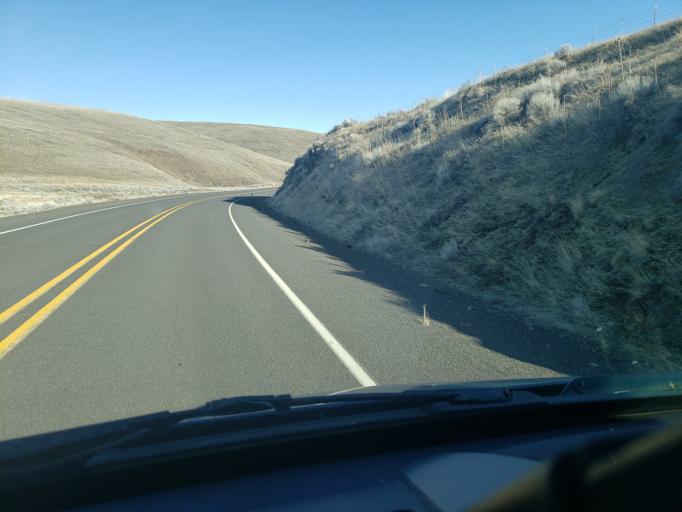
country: US
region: Oregon
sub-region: Umatilla County
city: Pilot Rock
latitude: 45.4673
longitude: -118.9146
